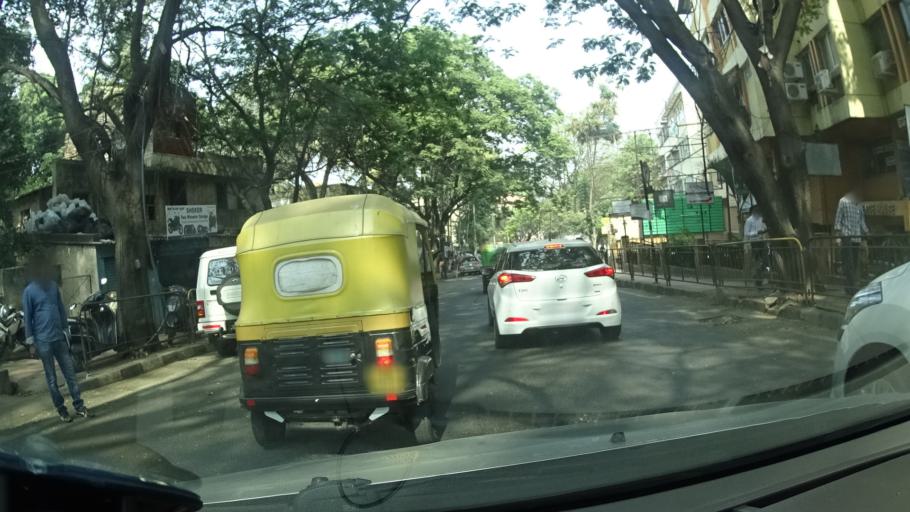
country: IN
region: Karnataka
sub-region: Bangalore Urban
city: Bangalore
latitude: 12.9898
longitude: 77.5929
